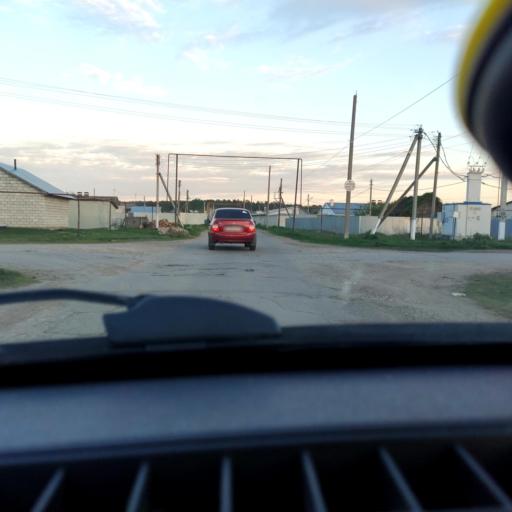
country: RU
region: Samara
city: Povolzhskiy
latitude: 53.6447
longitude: 49.6836
